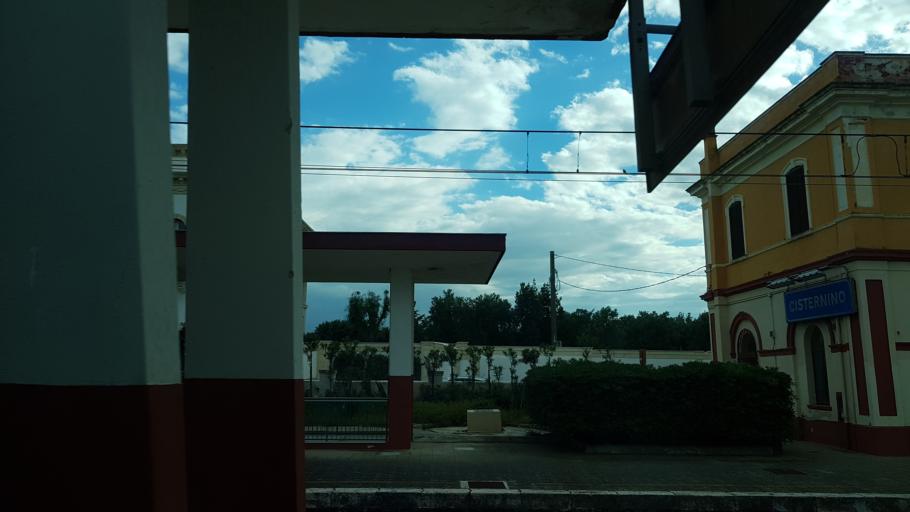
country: IT
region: Apulia
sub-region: Provincia di Brindisi
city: Pezze di Greco
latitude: 40.8165
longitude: 17.4571
